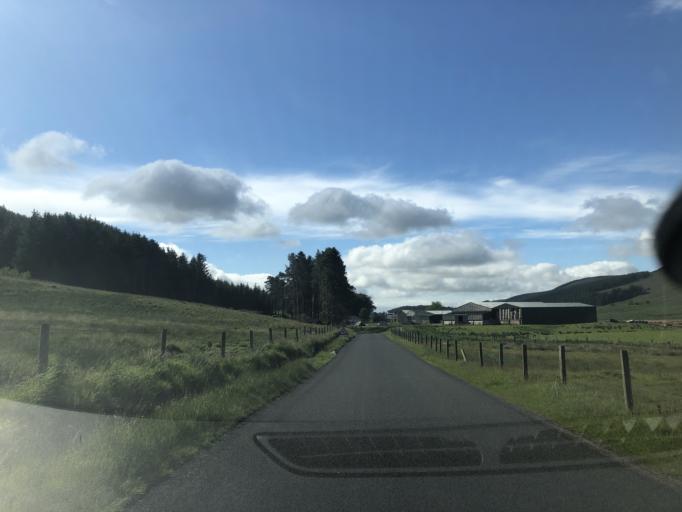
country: GB
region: Scotland
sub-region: Angus
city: Kirriemuir
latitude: 56.7945
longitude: -3.0350
